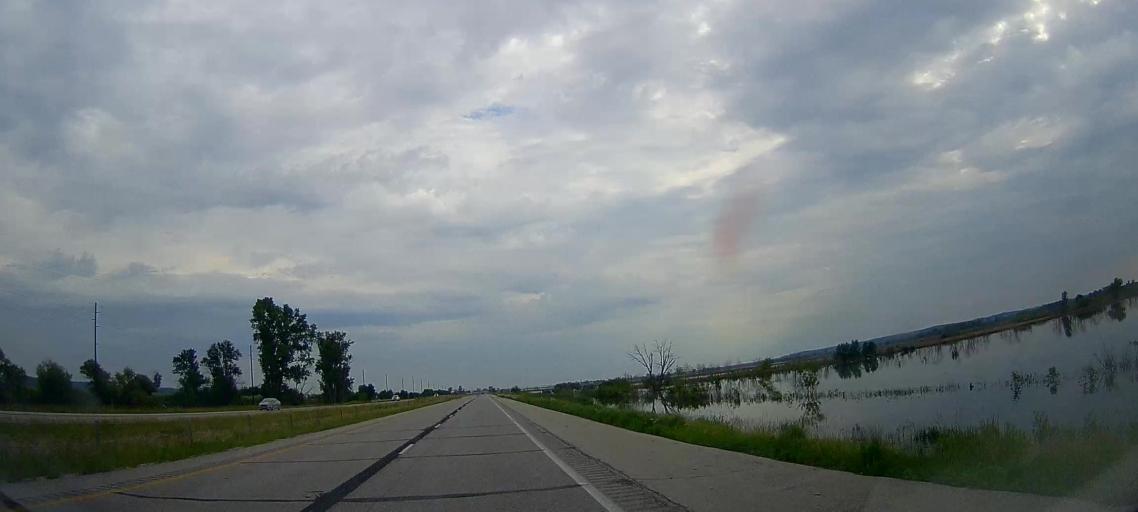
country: US
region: Iowa
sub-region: Harrison County
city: Missouri Valley
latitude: 41.4584
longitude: -95.8996
